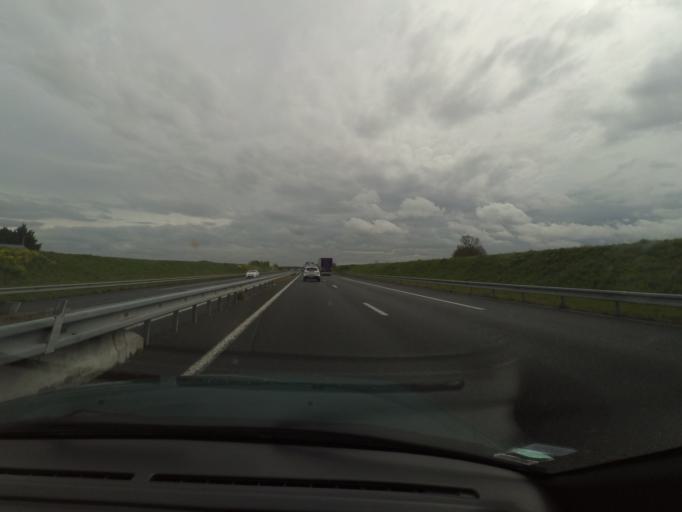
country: FR
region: Pays de la Loire
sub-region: Departement de Maine-et-Loire
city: Beaucouze
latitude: 47.4930
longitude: -0.6341
